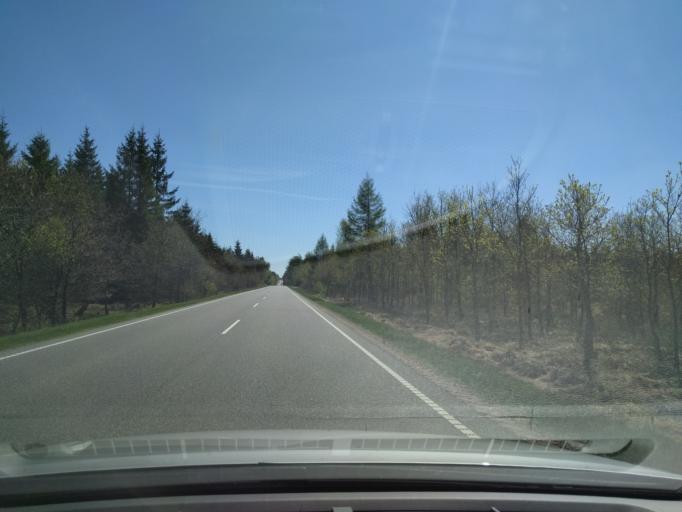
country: DK
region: South Denmark
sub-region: Billund Kommune
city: Billund
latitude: 55.6499
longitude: 9.0646
